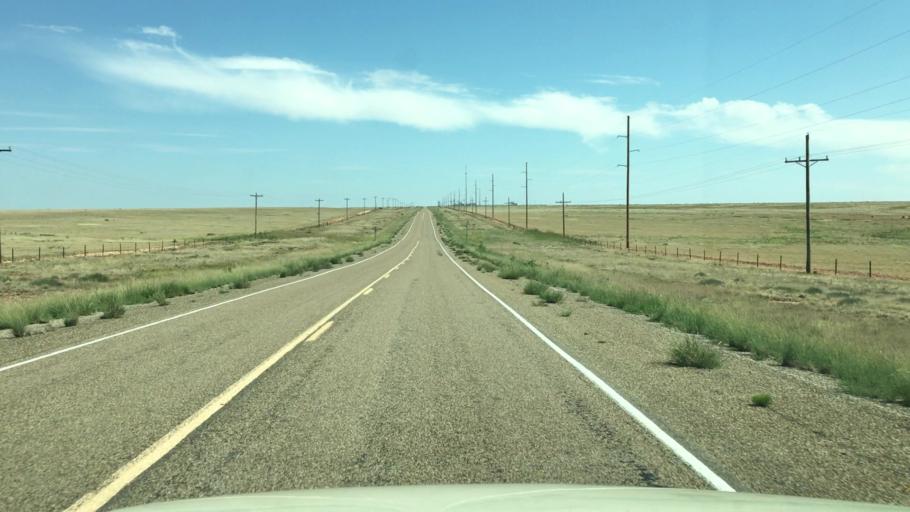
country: US
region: New Mexico
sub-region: Chaves County
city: Roswell
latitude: 33.9476
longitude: -104.5895
